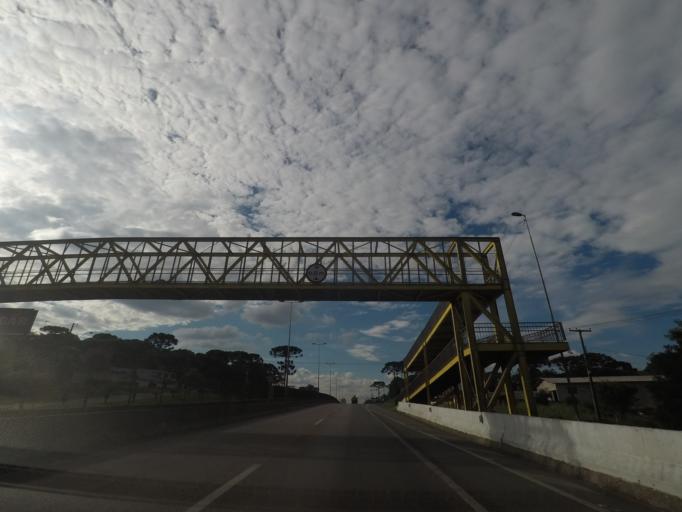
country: BR
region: Parana
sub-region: Araucaria
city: Araucaria
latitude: -25.6044
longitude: -49.3182
